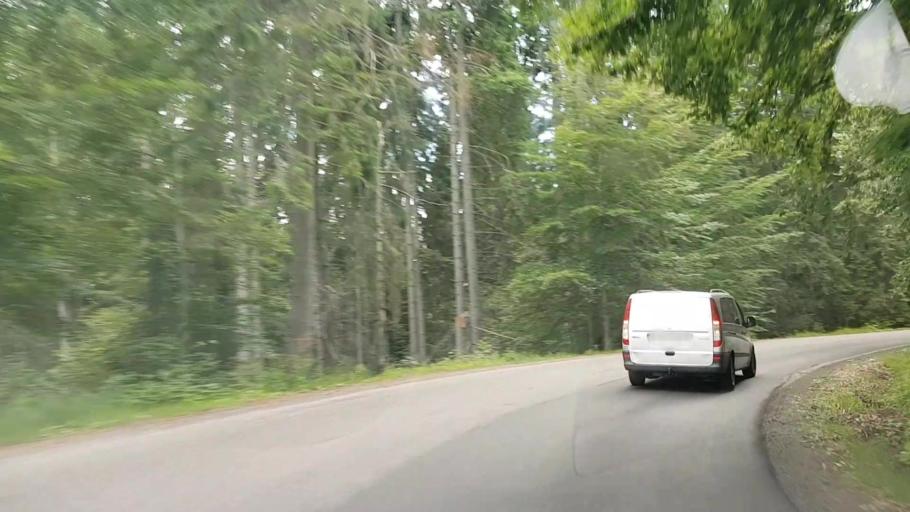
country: RO
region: Harghita
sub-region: Comuna Varsag
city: Varsag
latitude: 46.6660
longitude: 25.3203
